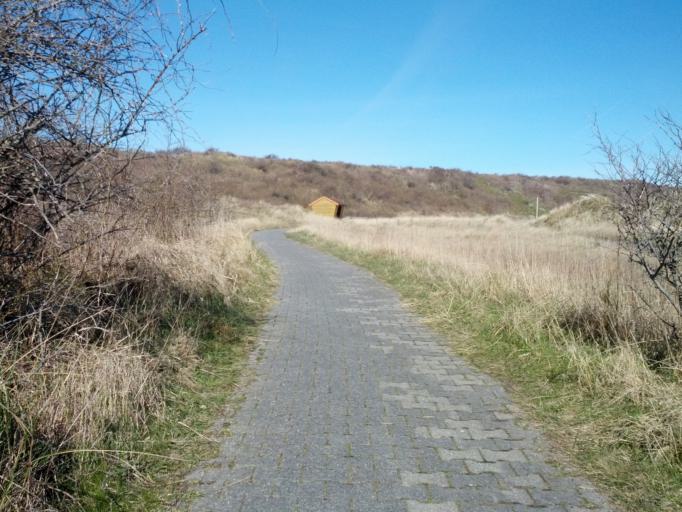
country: DE
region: Lower Saxony
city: Langeoog
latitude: 53.7536
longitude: 7.5186
